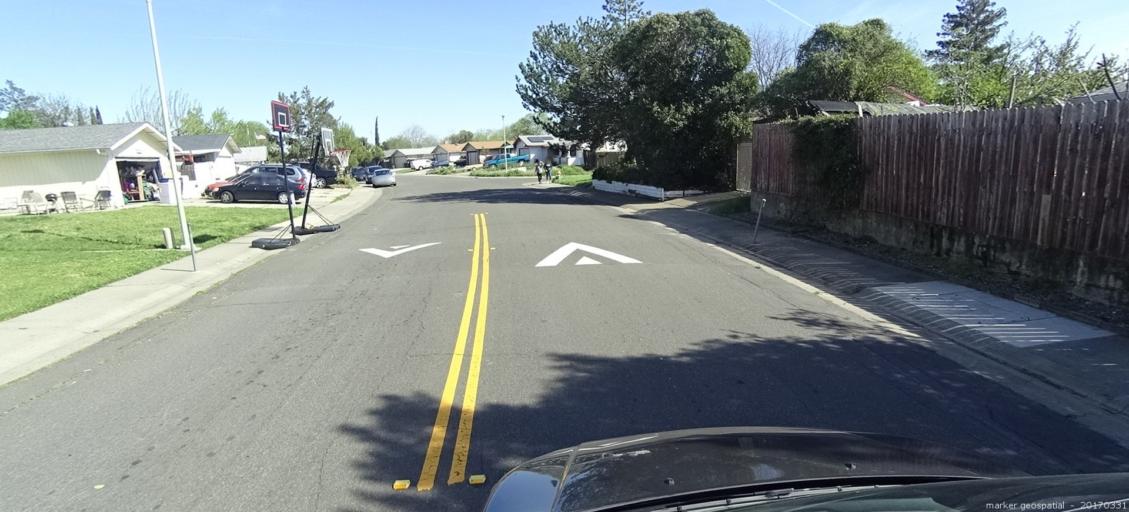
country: US
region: California
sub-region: Sacramento County
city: Laguna
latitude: 38.4539
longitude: -121.4420
